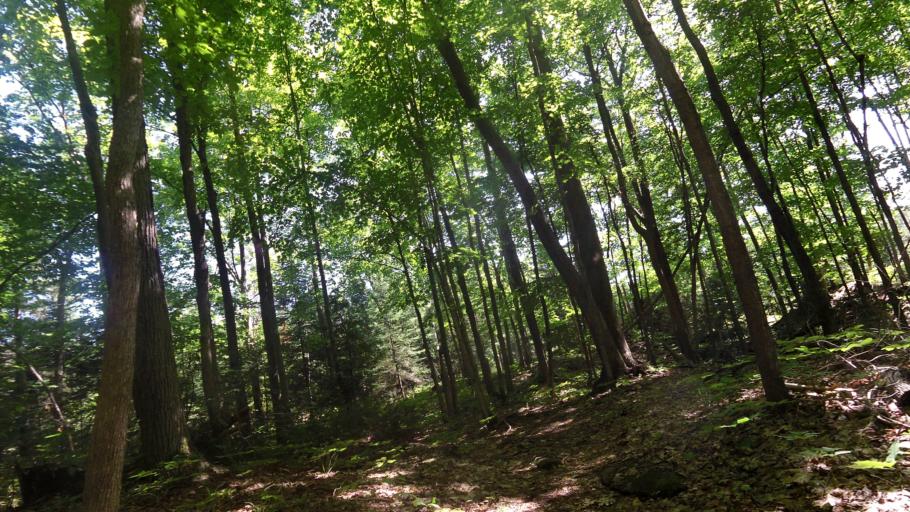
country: CA
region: Ontario
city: Arnprior
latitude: 45.4627
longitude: -76.2611
